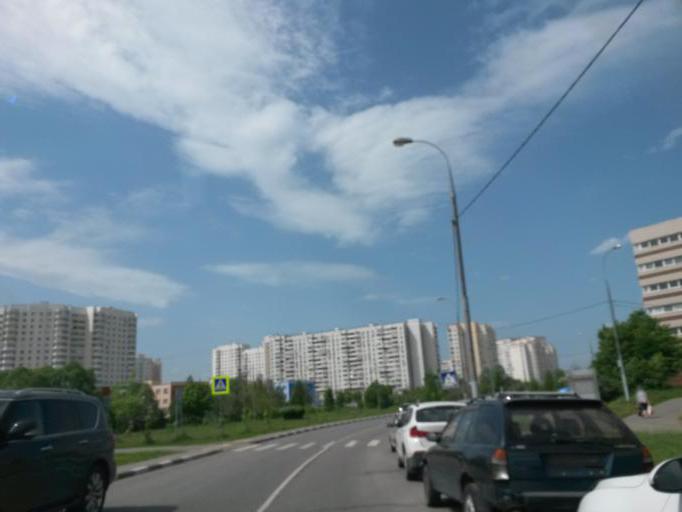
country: RU
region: Moskovskaya
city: Kommunarka
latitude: 55.5394
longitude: 37.5163
